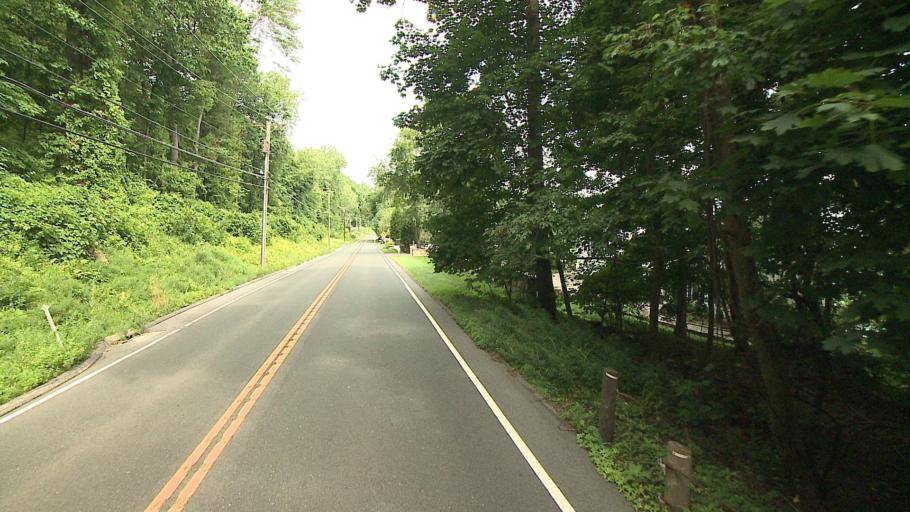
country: US
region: New York
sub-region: Putnam County
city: Putnam Lake
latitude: 41.4878
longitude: -73.4650
